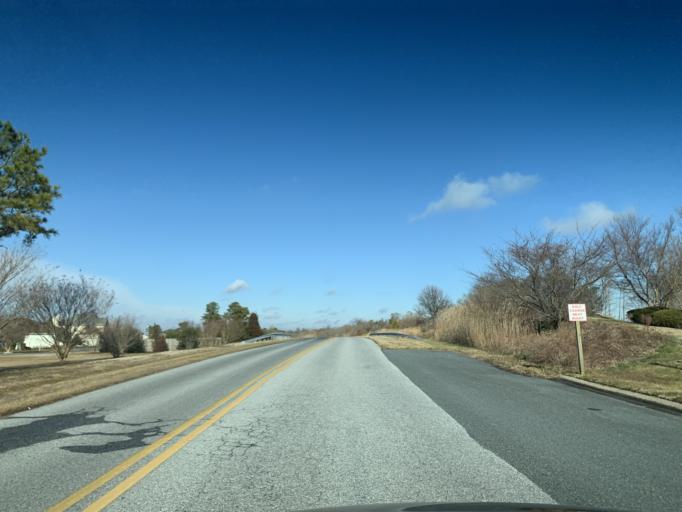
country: US
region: Maryland
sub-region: Worcester County
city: Ocean Pines
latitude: 38.4059
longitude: -75.1091
